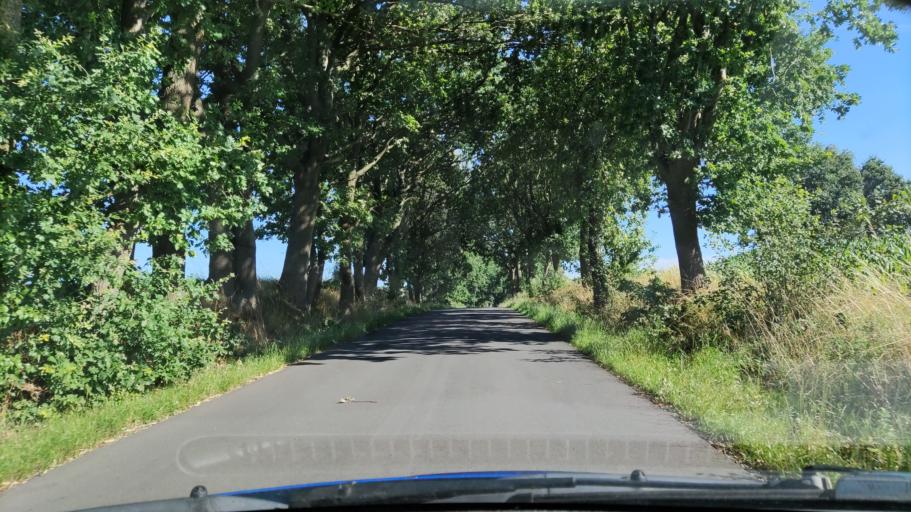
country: DE
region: Lower Saxony
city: Boitze
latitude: 53.1562
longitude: 10.7410
